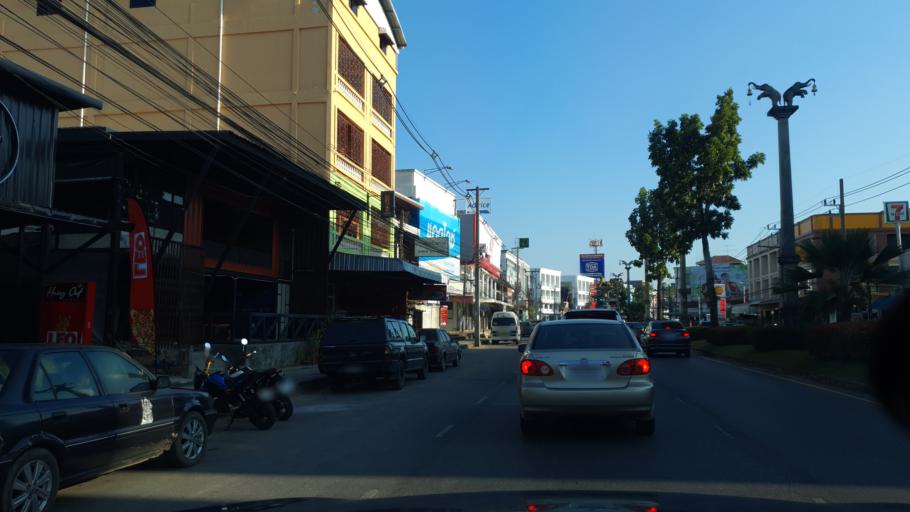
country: TH
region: Krabi
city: Krabi
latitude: 8.0681
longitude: 98.9142
